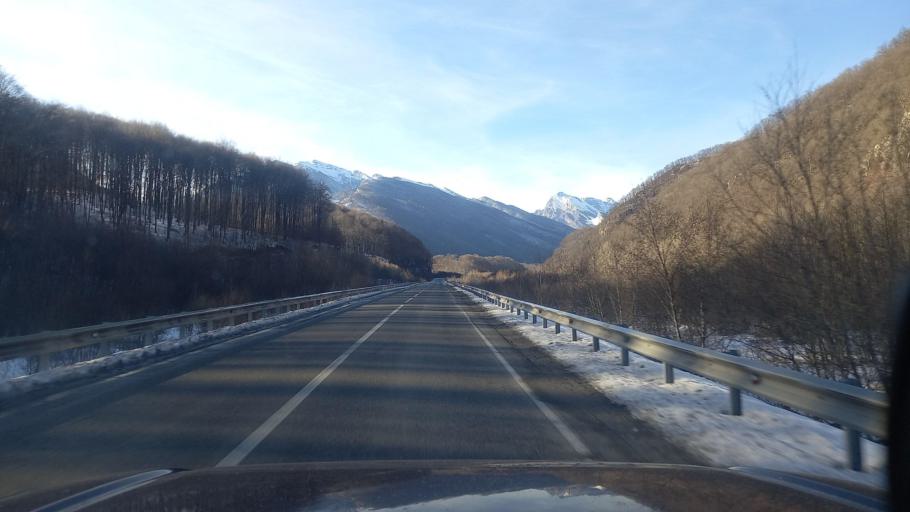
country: RU
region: North Ossetia
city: Gizel'
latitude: 42.9363
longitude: 44.5560
